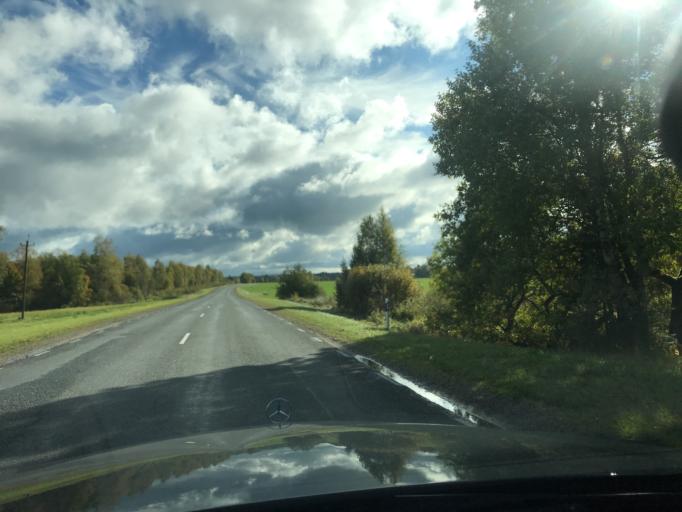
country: EE
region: Tartu
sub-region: Elva linn
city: Elva
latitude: 58.0083
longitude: 26.2533
